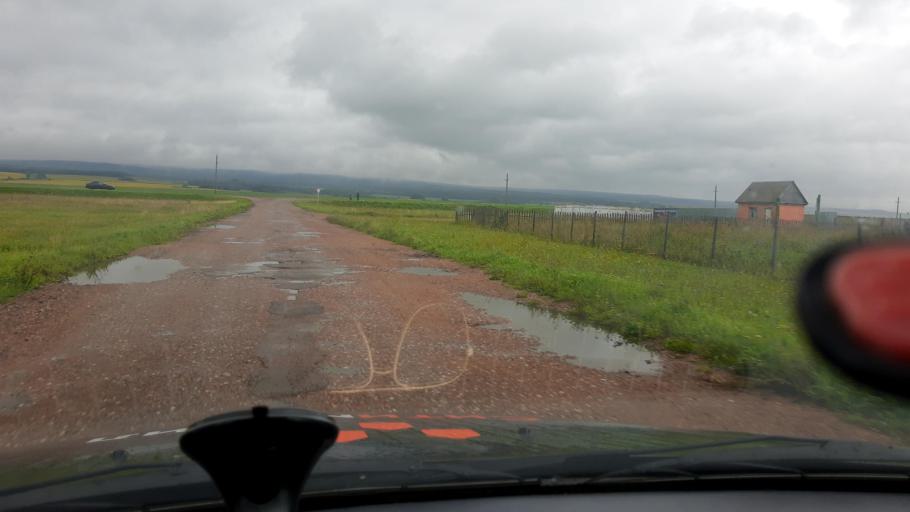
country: RU
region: Bashkortostan
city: Karmaskaly
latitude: 53.9896
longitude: 56.3960
